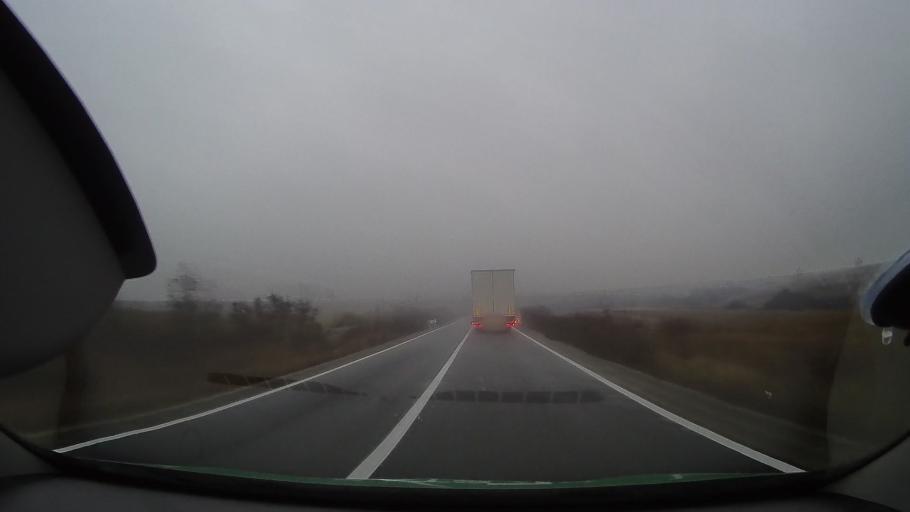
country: RO
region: Bihor
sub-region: Comuna Olcea
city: Olcea
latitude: 46.6622
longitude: 21.9626
